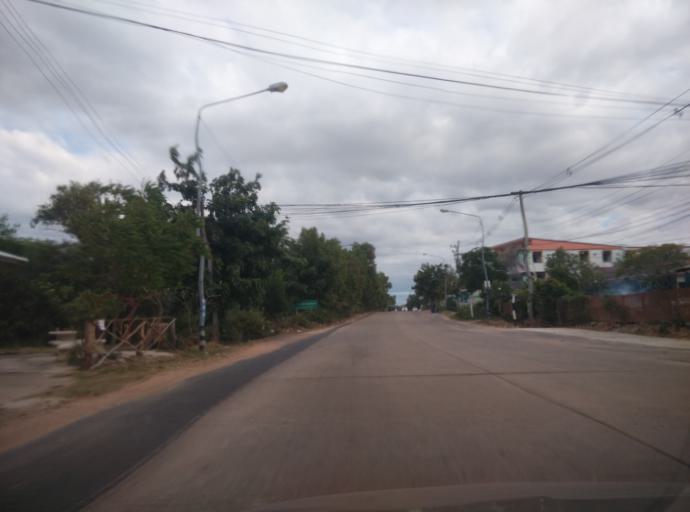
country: TH
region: Sisaket
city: Si Sa Ket
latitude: 15.1231
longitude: 104.3458
